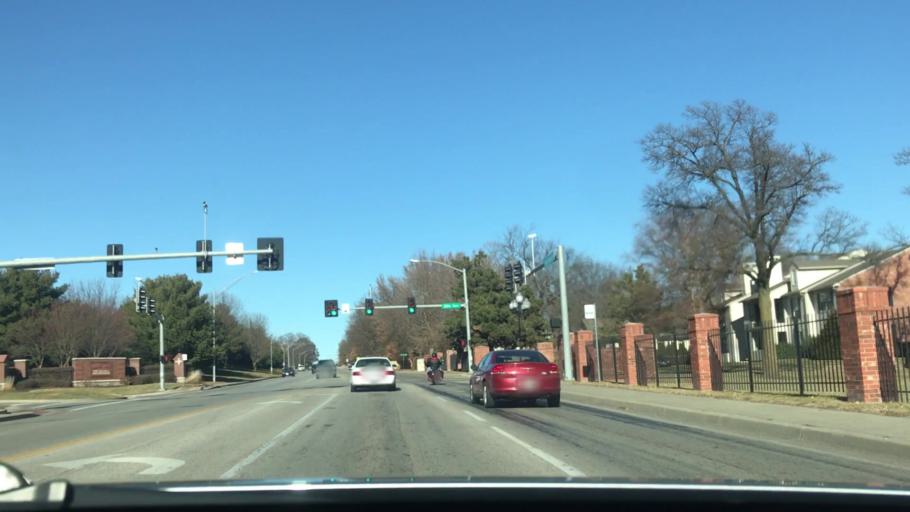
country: US
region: Missouri
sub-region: Jackson County
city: Independence
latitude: 39.0673
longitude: -94.3911
